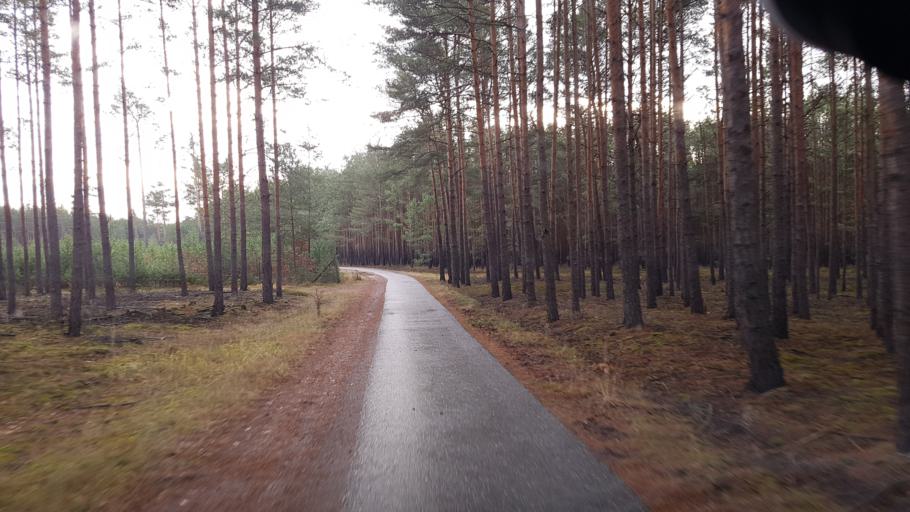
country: DE
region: Brandenburg
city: Lebusa
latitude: 51.7628
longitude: 13.4255
